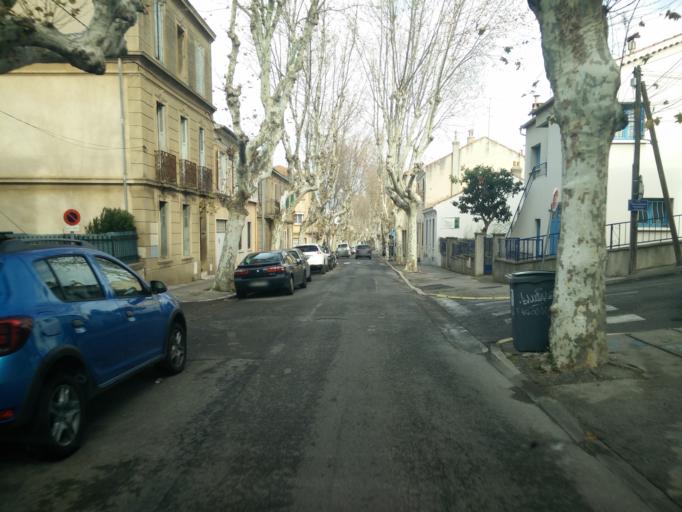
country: FR
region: Provence-Alpes-Cote d'Azur
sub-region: Departement du Var
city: La Seyne-sur-Mer
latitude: 43.0948
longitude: 5.8837
